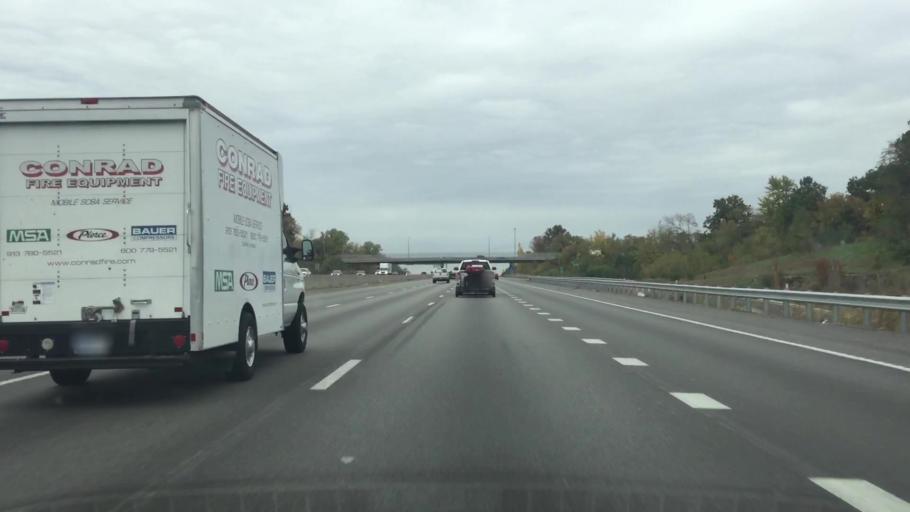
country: US
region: Missouri
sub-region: Jackson County
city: Raytown
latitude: 39.0327
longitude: -94.5002
